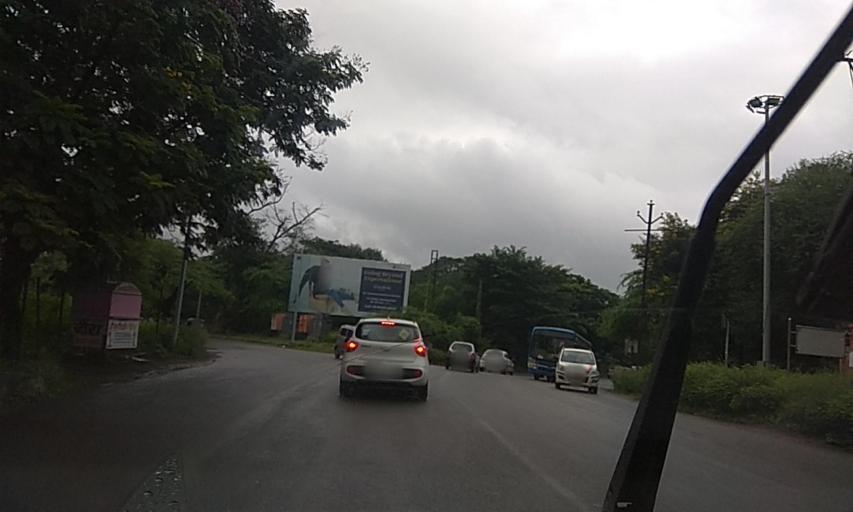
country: IN
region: Maharashtra
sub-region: Pune Division
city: Khadki
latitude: 18.5526
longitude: 73.8566
